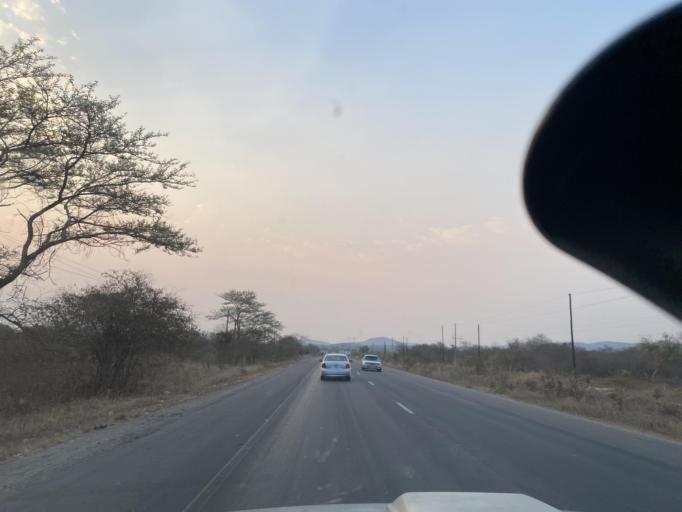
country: ZM
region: Lusaka
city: Kafue
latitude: -15.8294
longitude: 28.2325
